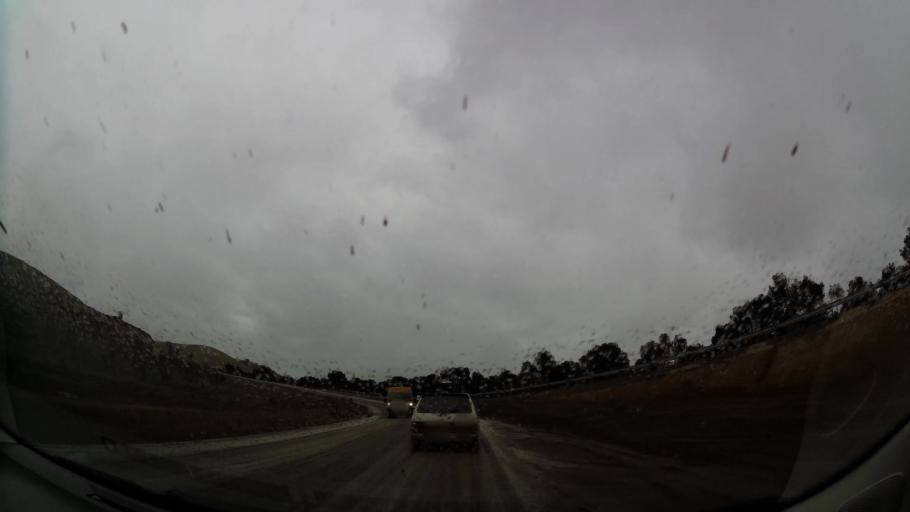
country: MA
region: Taza-Al Hoceima-Taounate
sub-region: Taza
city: Ajdir
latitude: 34.9023
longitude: -3.7913
